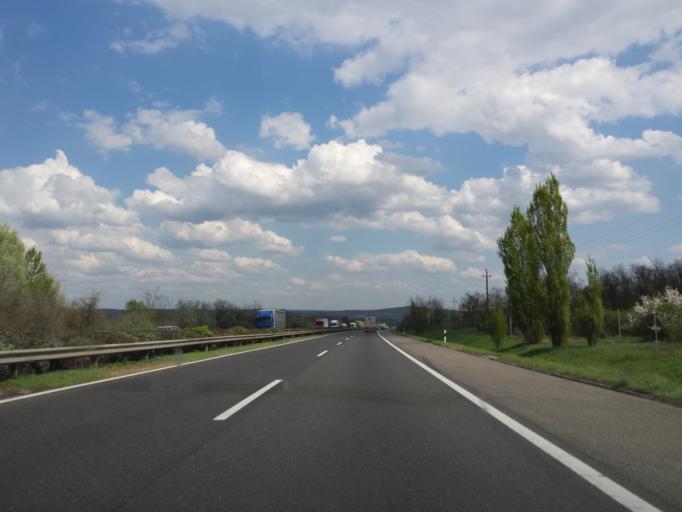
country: HU
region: Pest
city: Zsambek
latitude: 47.5100
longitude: 18.7450
